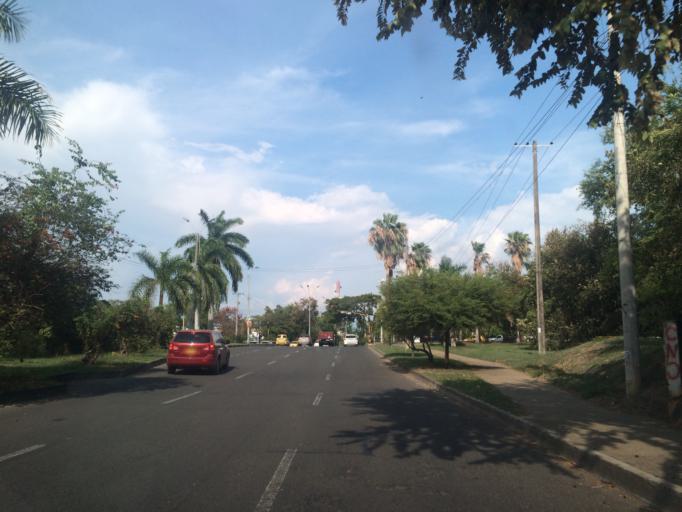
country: CO
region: Valle del Cauca
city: Cali
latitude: 3.3875
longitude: -76.5336
